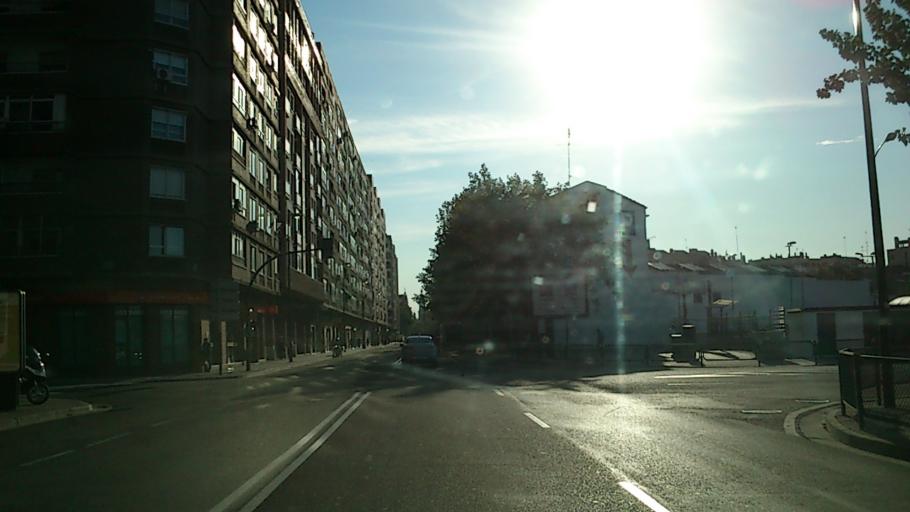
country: ES
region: Aragon
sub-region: Provincia de Zaragoza
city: Zaragoza
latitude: 41.6638
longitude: -0.8611
